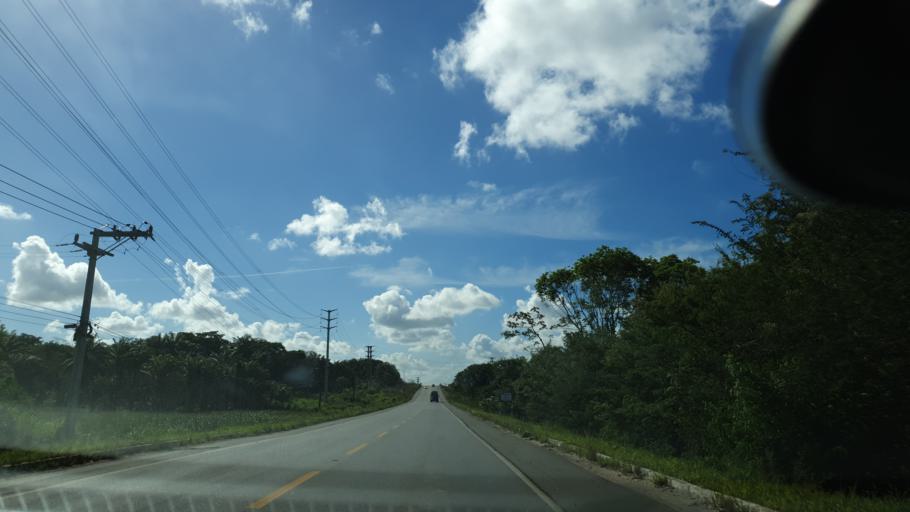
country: BR
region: Bahia
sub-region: Camacari
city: Camacari
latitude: -12.6830
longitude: -38.2358
